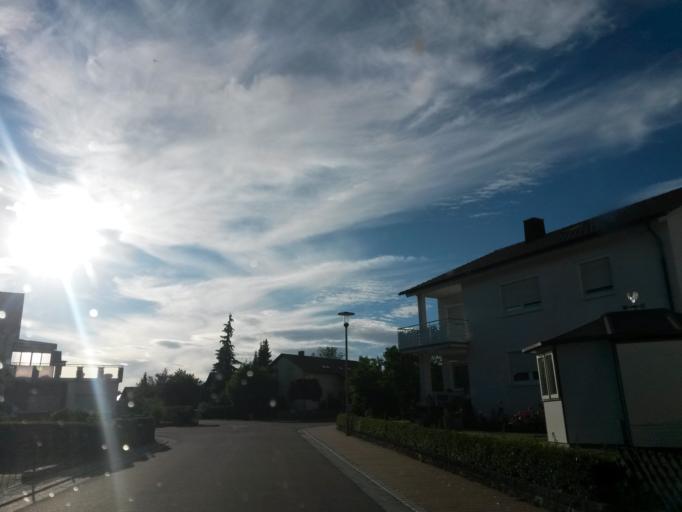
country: DE
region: Baden-Wuerttemberg
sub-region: Regierungsbezirk Stuttgart
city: Ellenberg
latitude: 49.0152
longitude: 10.2194
